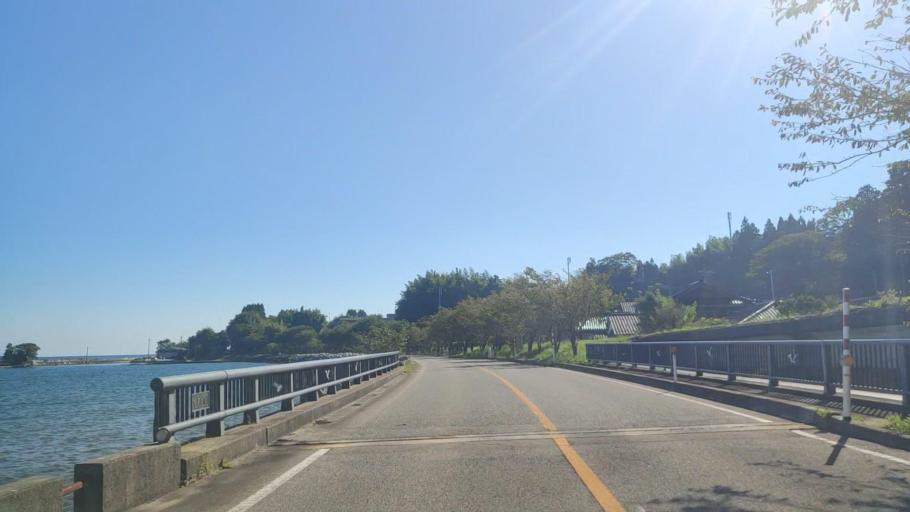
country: JP
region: Ishikawa
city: Nanao
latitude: 37.2775
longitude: 137.0973
